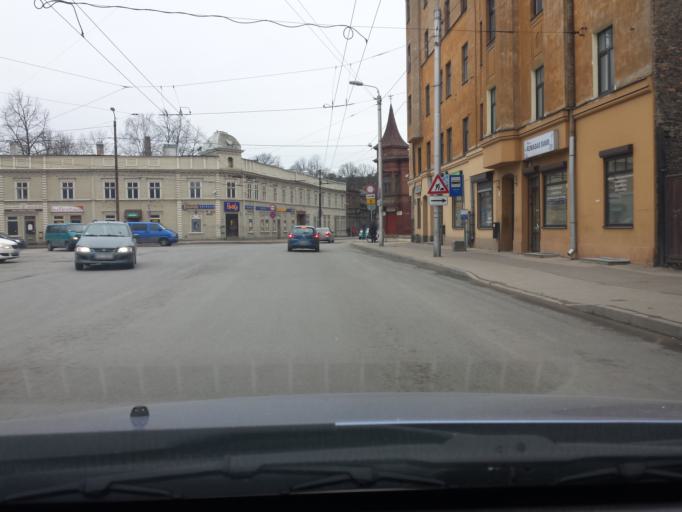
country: LV
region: Riga
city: Riga
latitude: 56.9539
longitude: 24.1472
